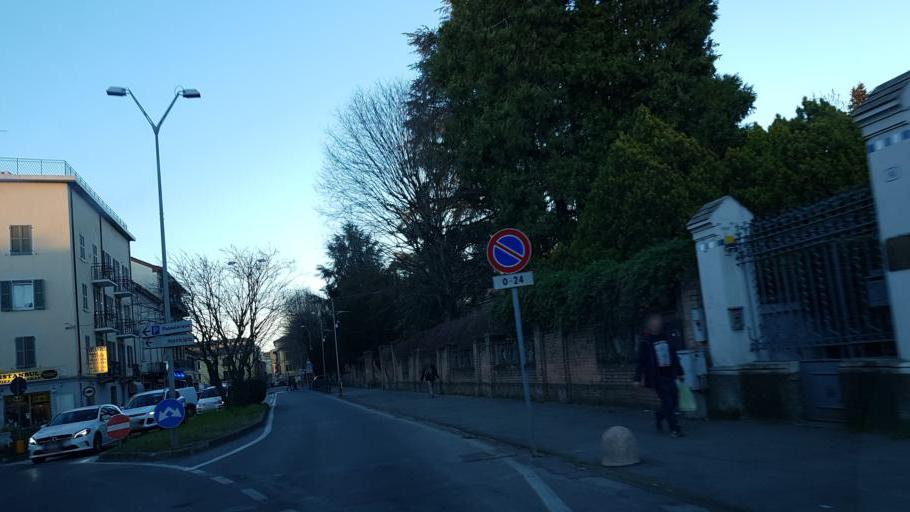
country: IT
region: Piedmont
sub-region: Provincia di Alessandria
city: Tortona
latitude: 44.8922
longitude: 8.8615
